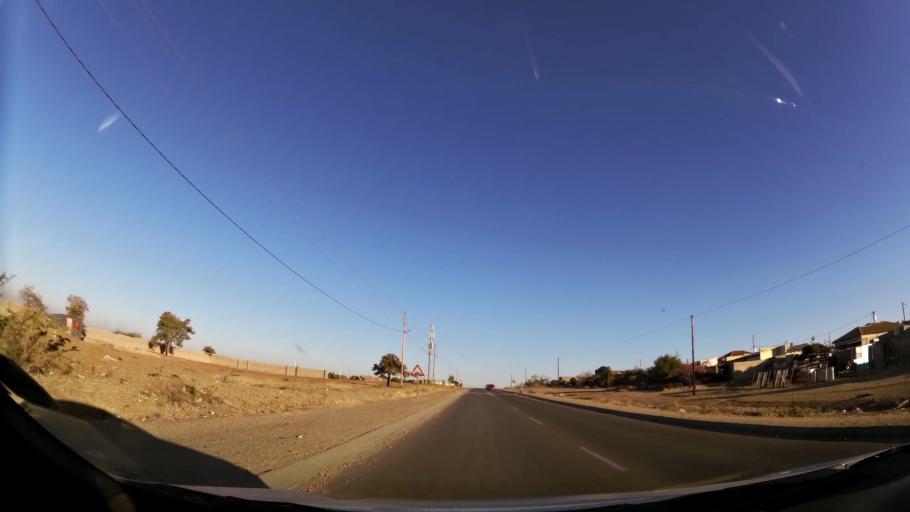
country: ZA
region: Limpopo
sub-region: Capricorn District Municipality
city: Polokwane
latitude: -23.8437
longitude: 29.3531
